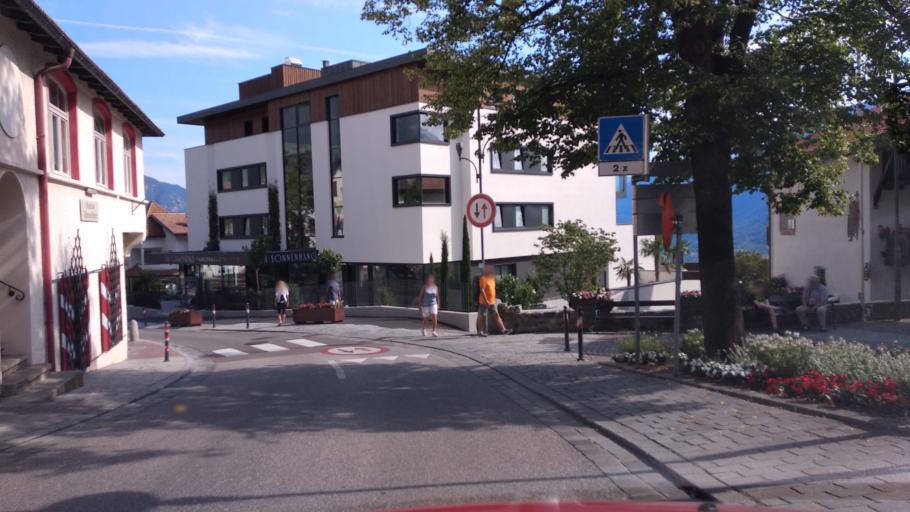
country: IT
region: Trentino-Alto Adige
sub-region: Bolzano
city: Tirolo
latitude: 46.6905
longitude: 11.1542
